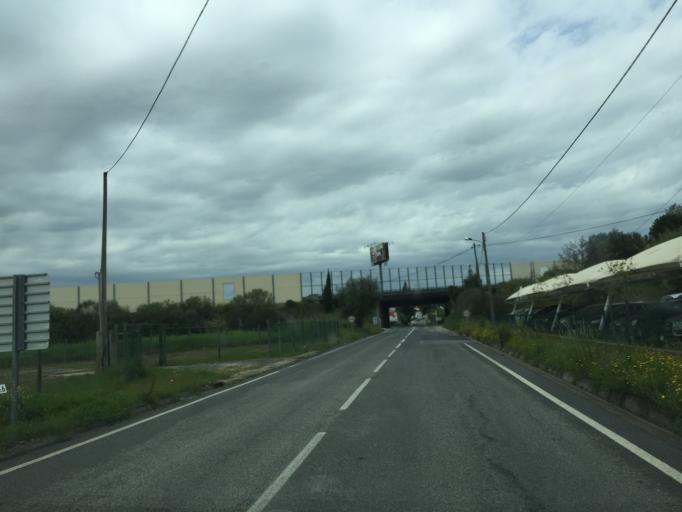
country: PT
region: Lisbon
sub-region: Azambuja
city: Aveiras de Cima
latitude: 39.1317
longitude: -8.8953
